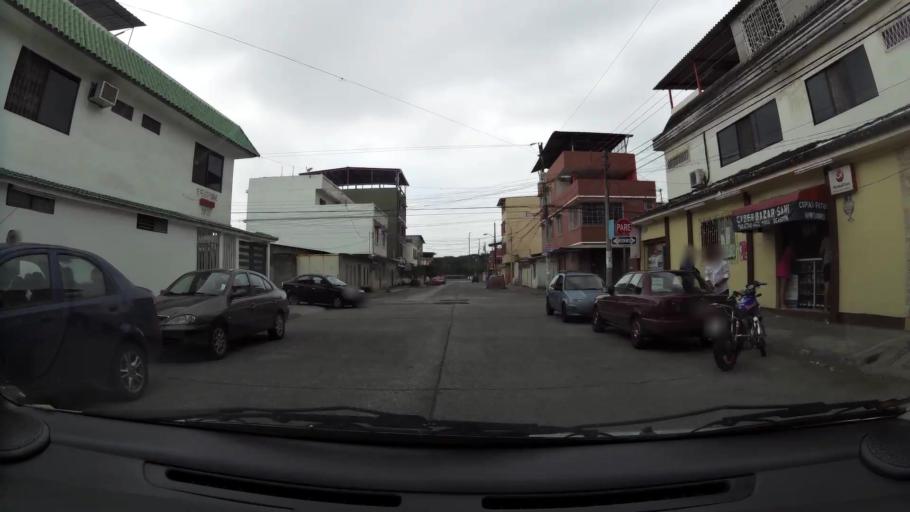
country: EC
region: Guayas
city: Eloy Alfaro
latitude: -2.1225
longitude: -79.8844
